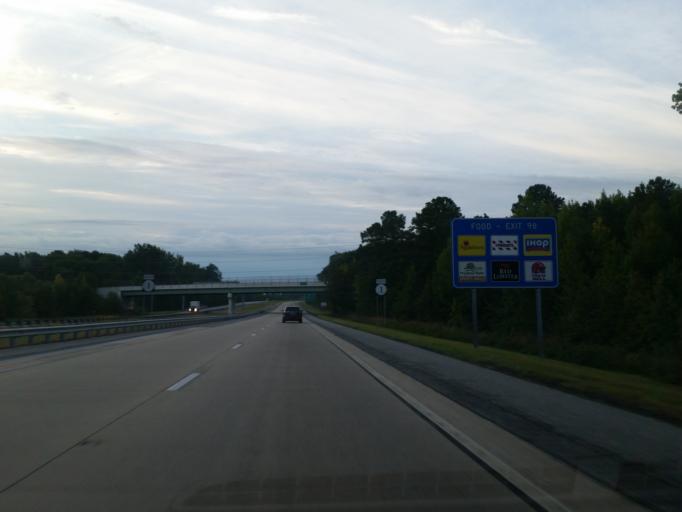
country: US
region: Delaware
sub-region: Kent County
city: Dover
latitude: 39.1779
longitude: -75.5045
